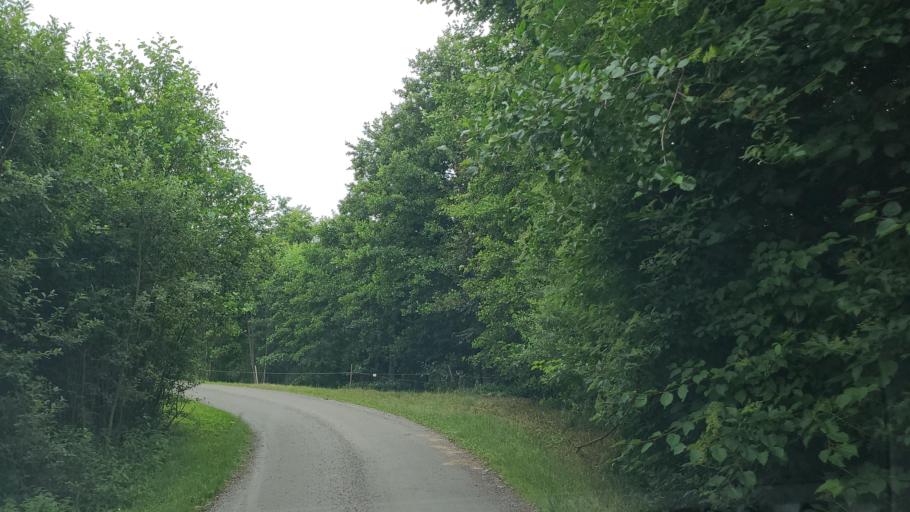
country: SE
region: Stockholm
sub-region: Upplands-Bro Kommun
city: Bro
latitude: 59.4654
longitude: 17.5873
